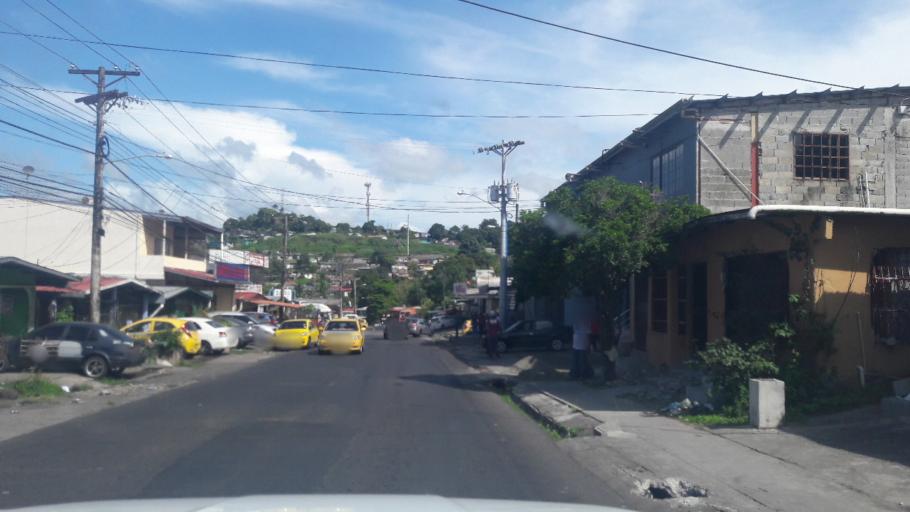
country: PA
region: Panama
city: San Miguelito
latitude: 9.0675
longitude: -79.4880
